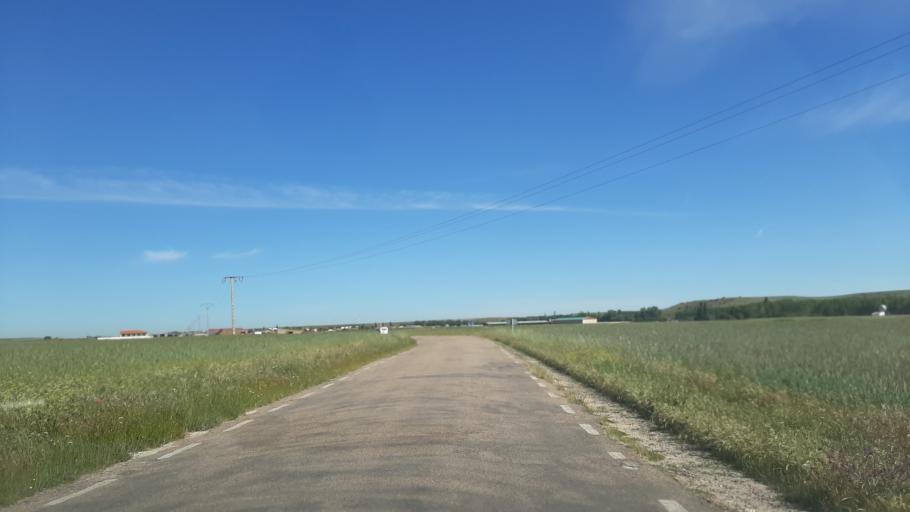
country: ES
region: Castille and Leon
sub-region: Provincia de Salamanca
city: Pedrosillo de Alba
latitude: 40.8114
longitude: -5.3847
